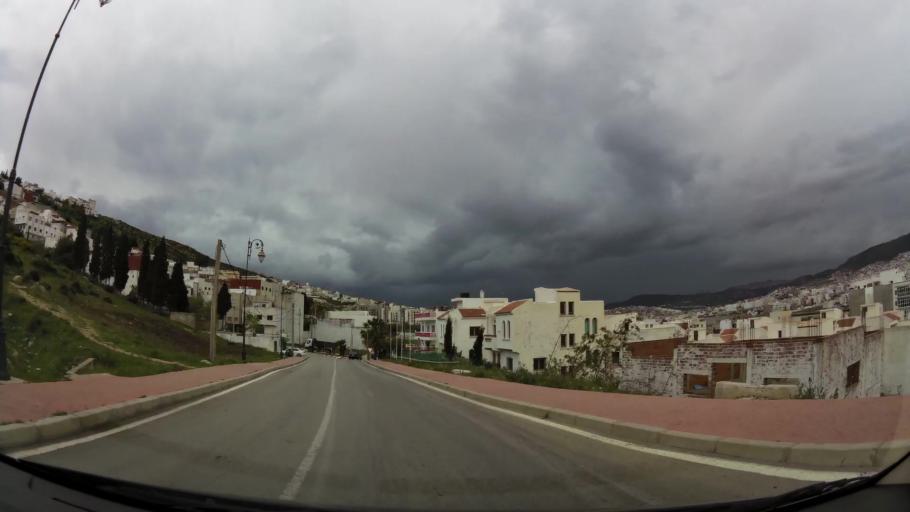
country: MA
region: Tanger-Tetouan
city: Tetouan
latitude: 35.5556
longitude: -5.3755
